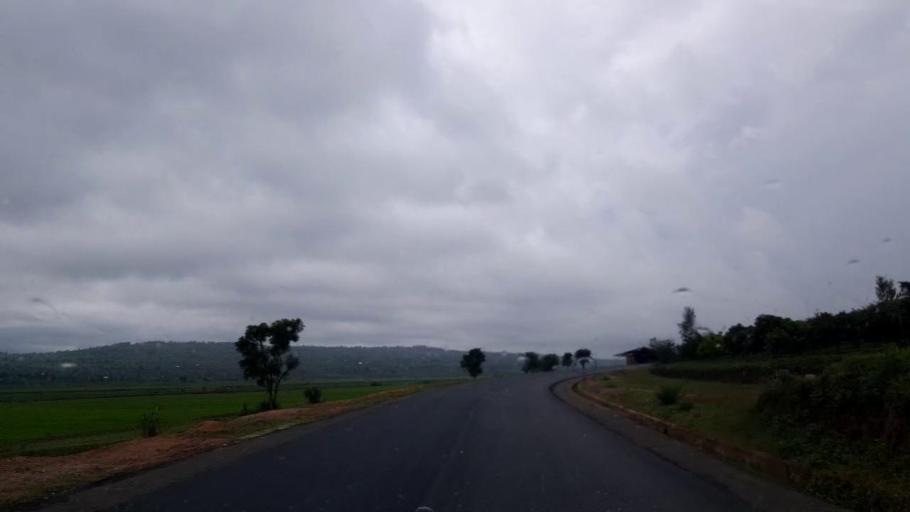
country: RW
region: Northern Province
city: Byumba
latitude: -1.4073
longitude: 30.2849
